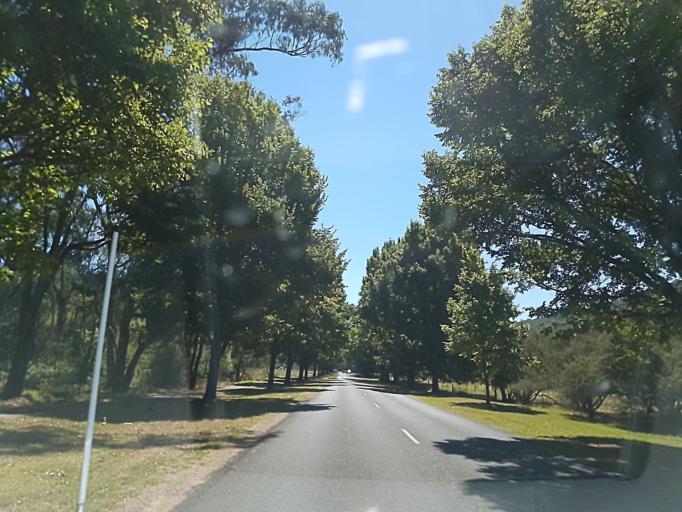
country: AU
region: Victoria
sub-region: Alpine
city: Mount Beauty
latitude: -36.7495
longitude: 146.9805
